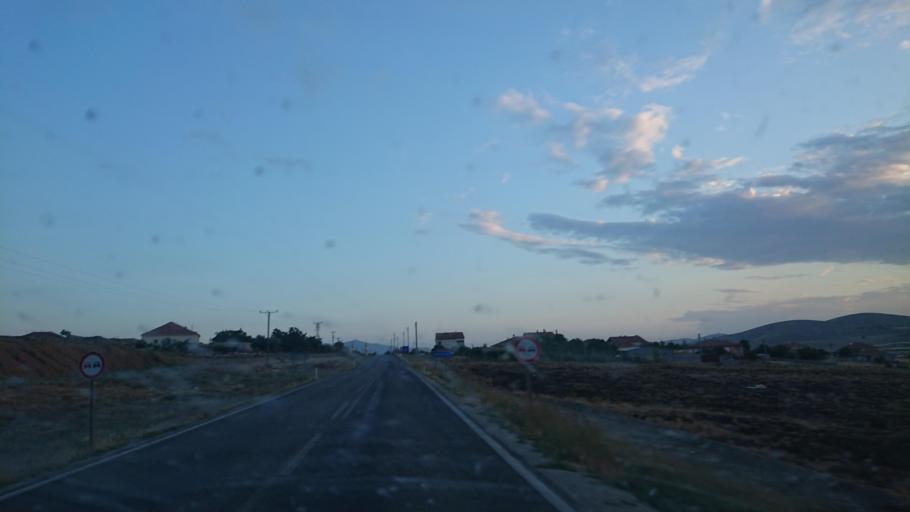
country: TR
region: Aksaray
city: Balci
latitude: 38.7973
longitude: 34.1273
